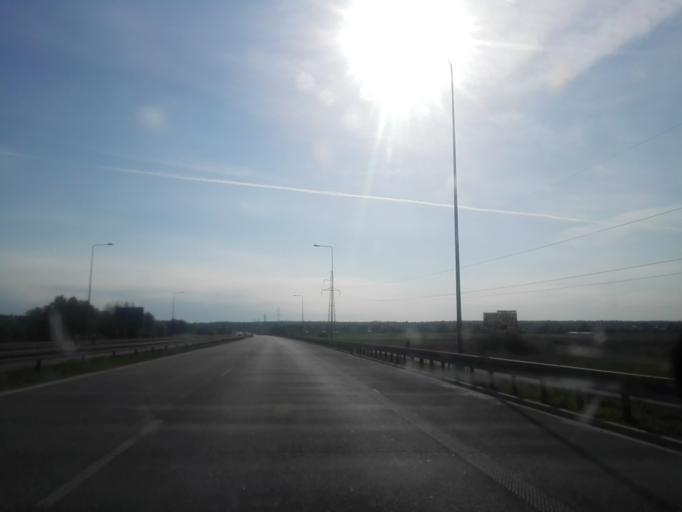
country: PL
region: Lodz Voivodeship
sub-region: Piotrkow Trybunalski
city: Piotrkow Trybunalski
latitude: 51.4436
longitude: 19.7355
